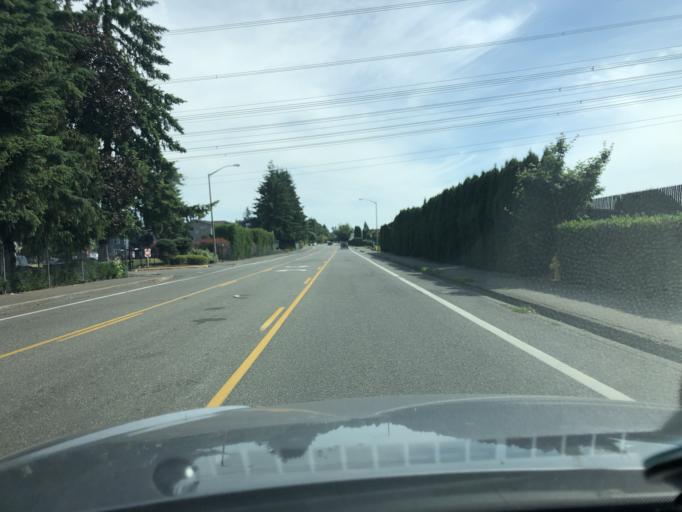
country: US
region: Washington
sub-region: King County
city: Auburn
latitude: 47.3378
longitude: -122.2194
